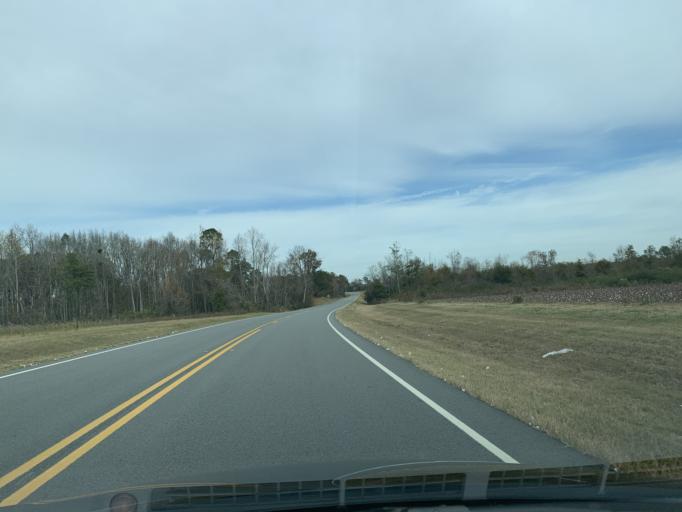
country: US
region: Georgia
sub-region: Wilcox County
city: Rochelle
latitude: 31.8391
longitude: -83.4284
